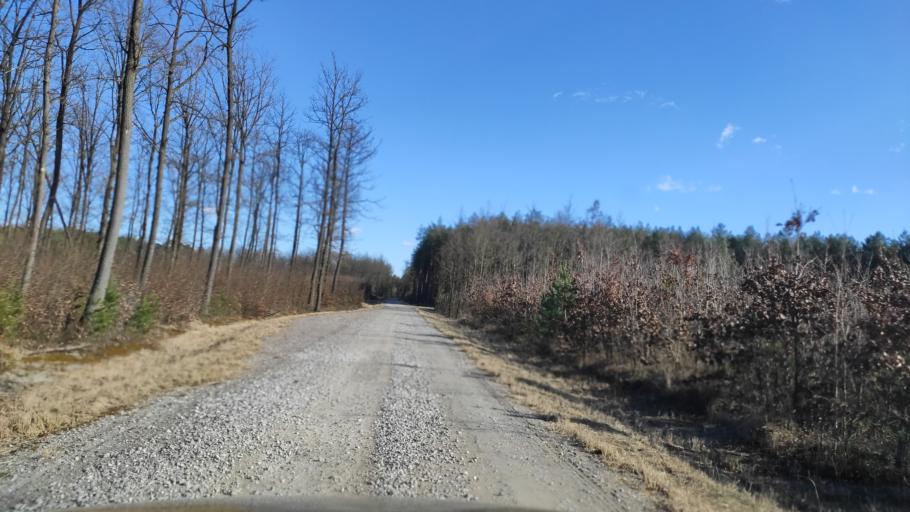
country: PL
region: Masovian Voivodeship
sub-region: Powiat radomski
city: Jedlnia-Letnisko
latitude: 51.4510
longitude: 21.2870
